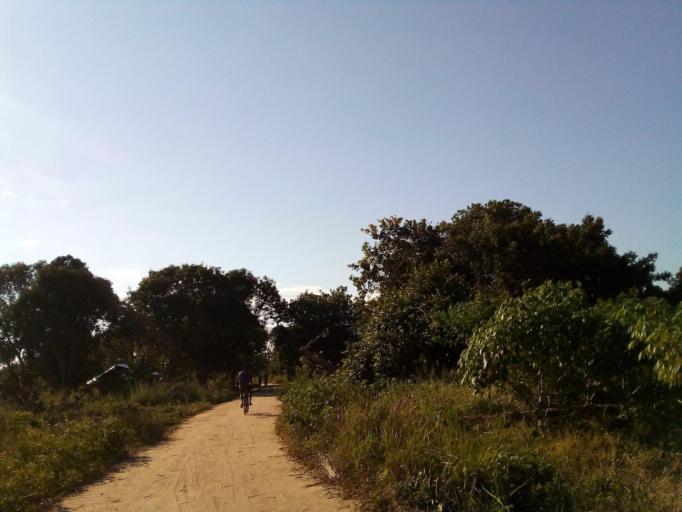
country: MZ
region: Zambezia
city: Quelimane
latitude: -17.5176
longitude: 36.6858
